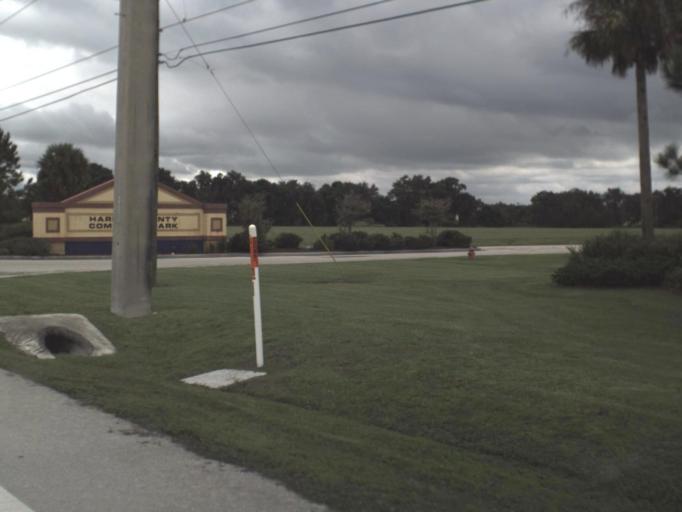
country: US
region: Florida
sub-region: Hardee County
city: Bowling Green
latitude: 27.5949
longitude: -81.8324
